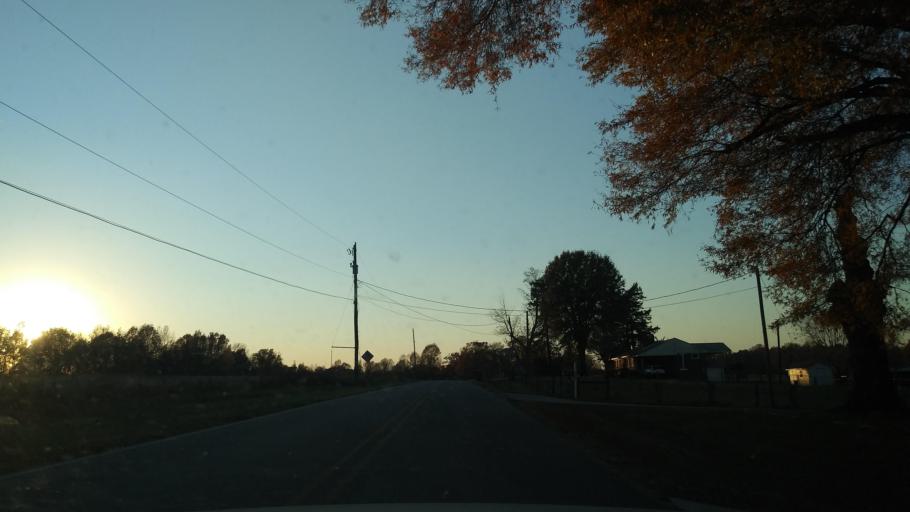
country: US
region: North Carolina
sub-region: Guilford County
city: Pleasant Garden
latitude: 36.0008
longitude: -79.7727
